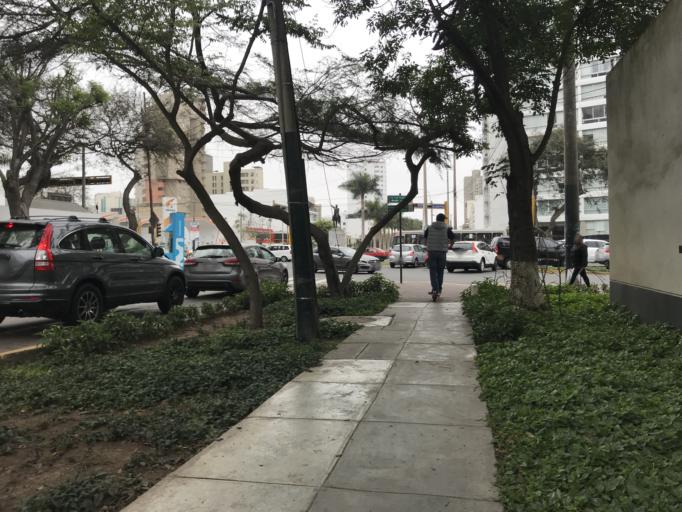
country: PE
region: Lima
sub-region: Lima
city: San Isidro
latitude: -12.0942
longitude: -77.0508
